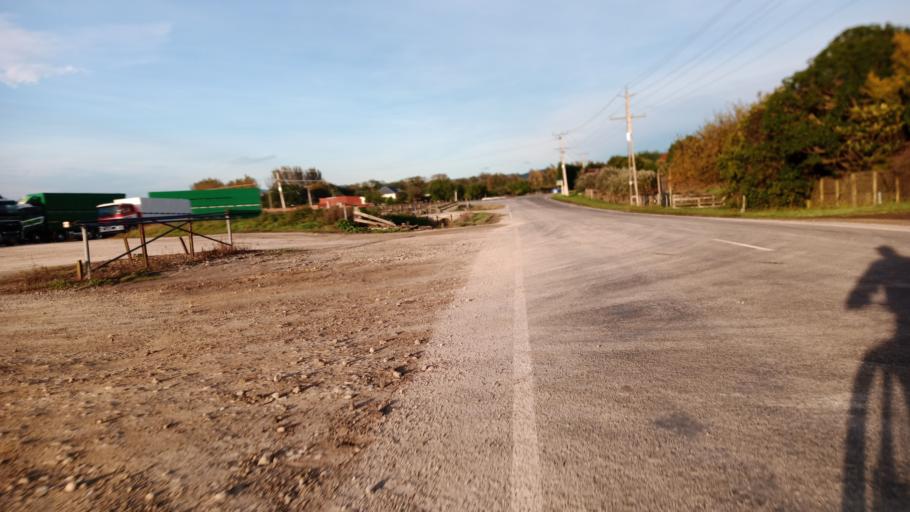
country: NZ
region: Gisborne
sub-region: Gisborne District
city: Gisborne
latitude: -38.6507
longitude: 177.9435
